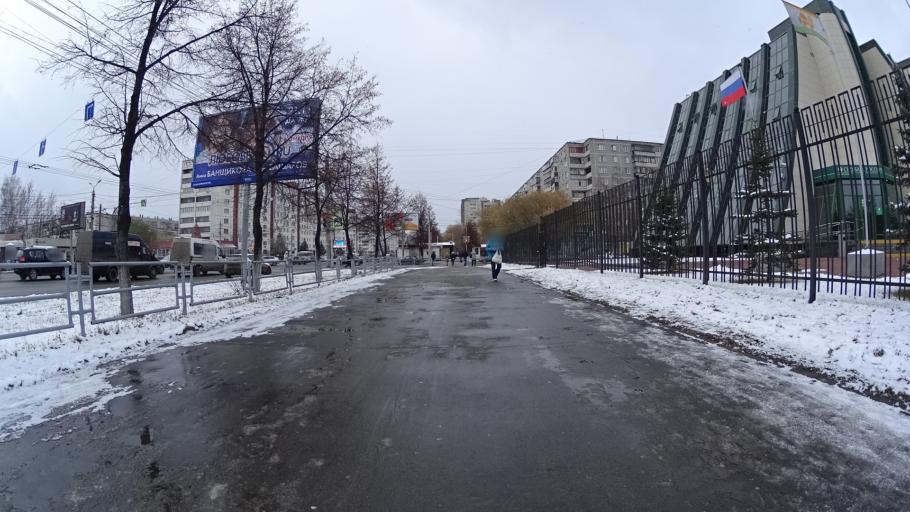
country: RU
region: Chelyabinsk
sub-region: Gorod Chelyabinsk
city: Chelyabinsk
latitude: 55.1946
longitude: 61.3189
